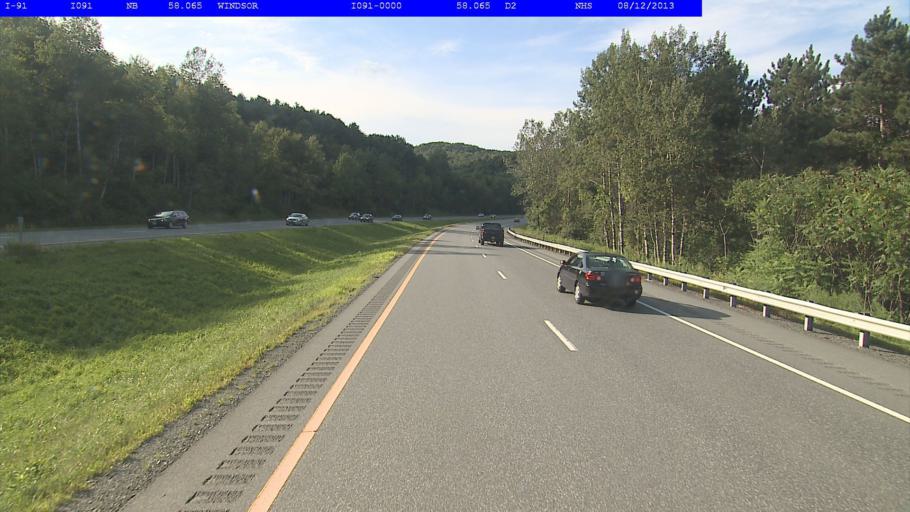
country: US
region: Vermont
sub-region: Windsor County
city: Windsor
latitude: 43.4956
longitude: -72.4099
